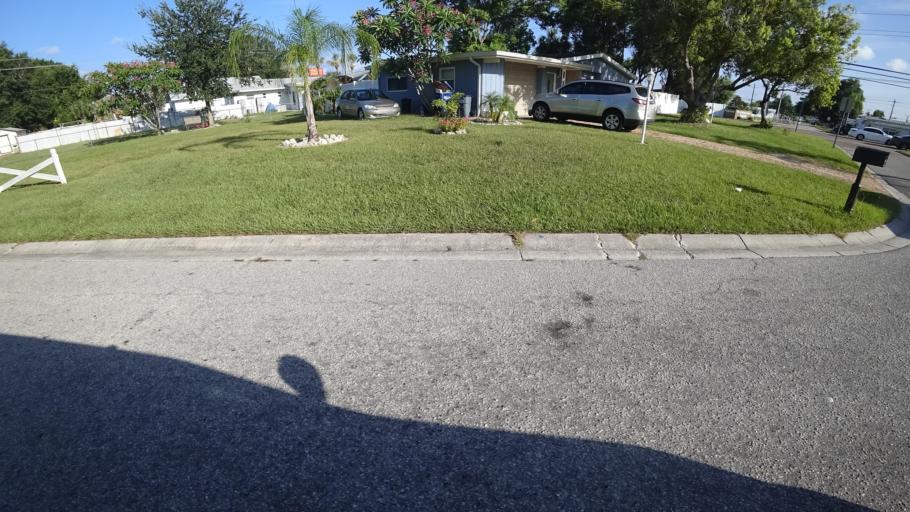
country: US
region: Florida
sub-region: Manatee County
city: South Bradenton
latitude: 27.4473
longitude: -82.5654
